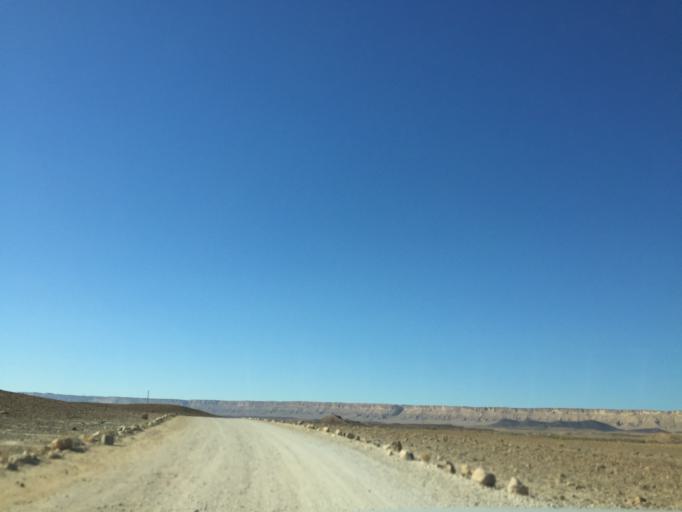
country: IL
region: Southern District
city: Mitzpe Ramon
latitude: 30.6243
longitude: 34.9248
